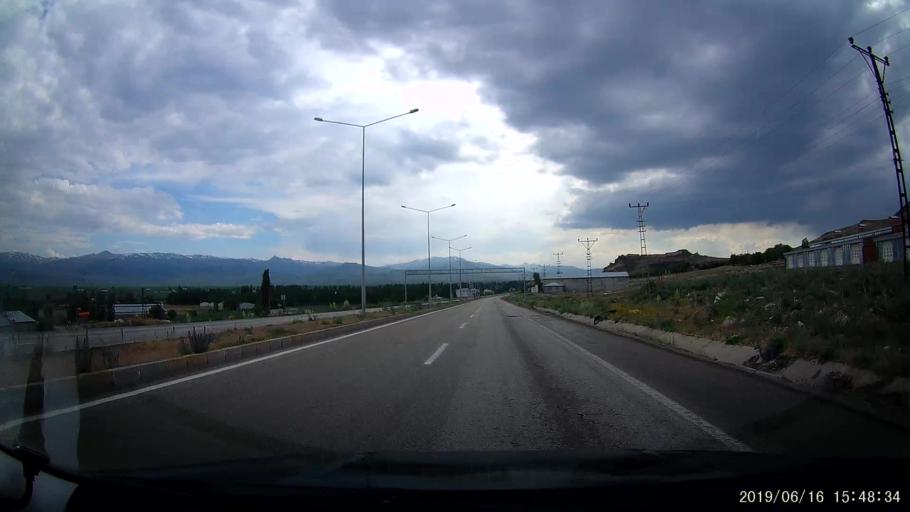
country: TR
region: Erzurum
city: Pasinler
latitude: 39.9818
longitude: 41.6986
